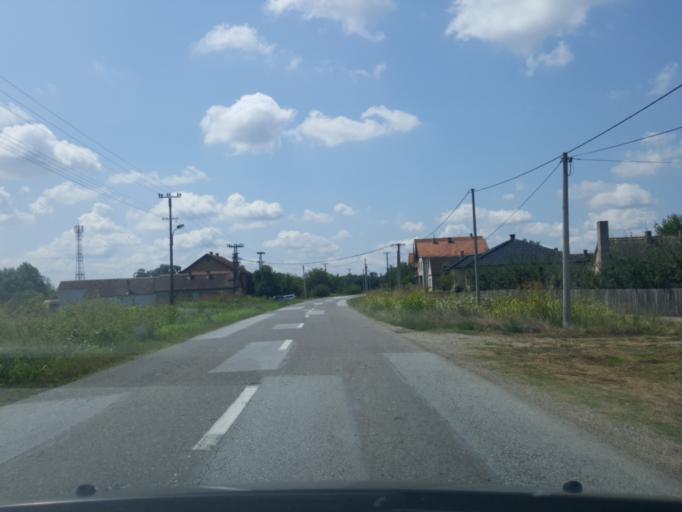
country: RS
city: Salas Nocajski
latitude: 44.9330
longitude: 19.5684
